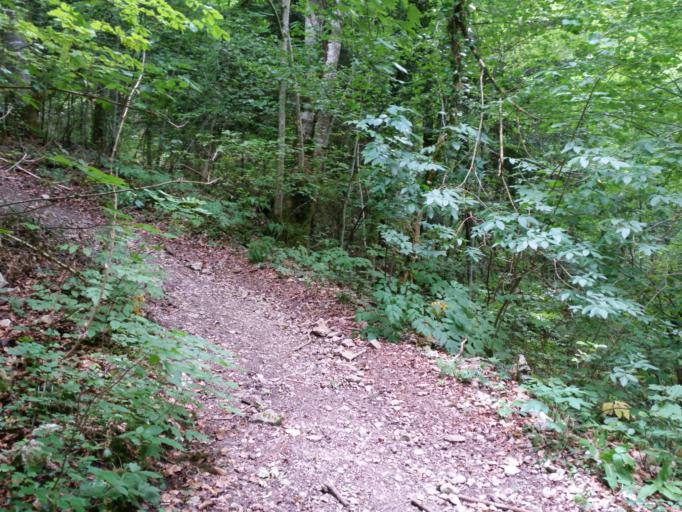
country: FR
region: Franche-Comte
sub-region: Departement du Jura
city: Salins-les-Bains
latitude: 46.9660
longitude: 5.9952
